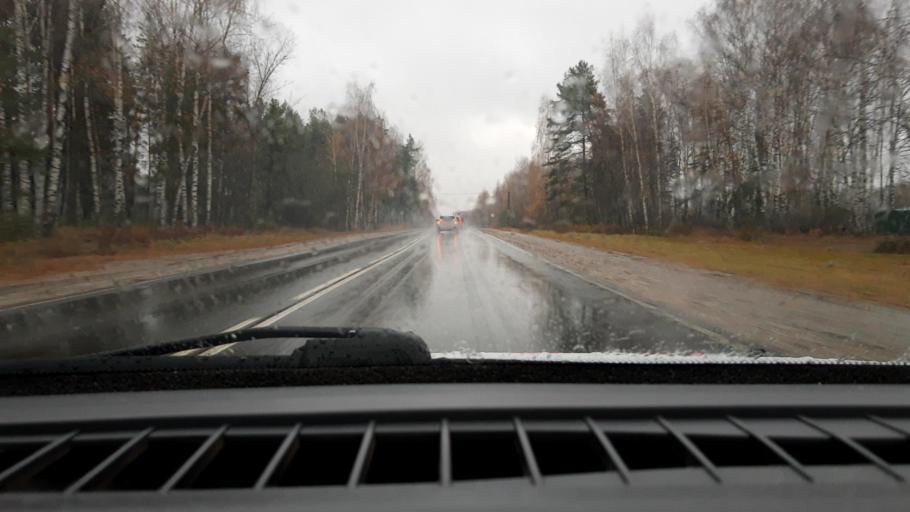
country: RU
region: Nizjnij Novgorod
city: Sitniki
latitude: 56.4547
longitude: 44.0199
